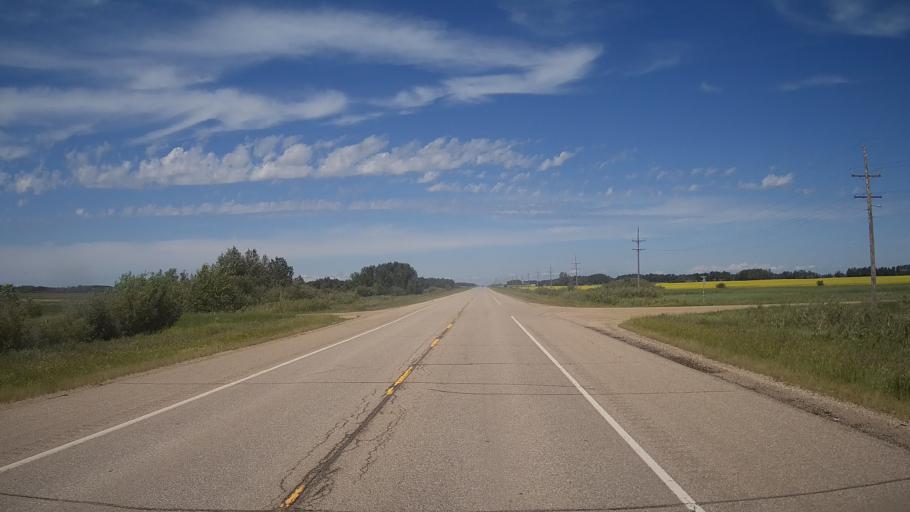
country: CA
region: Saskatchewan
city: Langenburg
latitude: 50.6525
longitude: -101.2760
